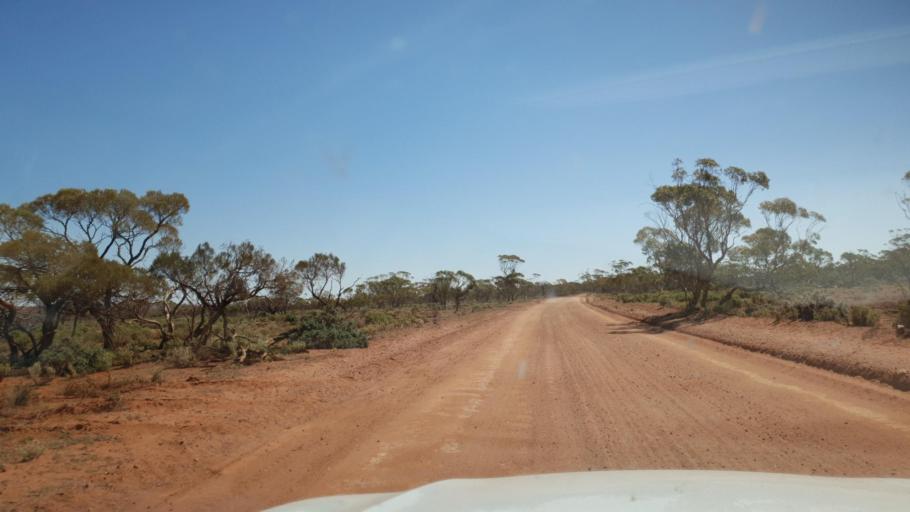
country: AU
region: South Australia
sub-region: Whyalla
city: Whyalla
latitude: -32.6205
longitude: 136.7723
